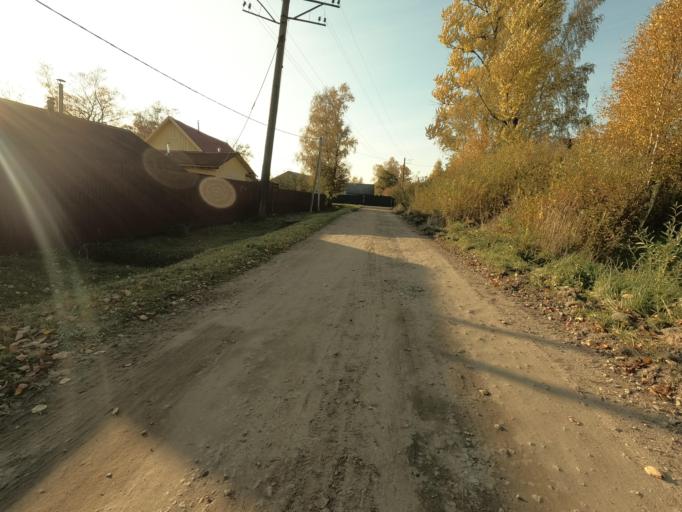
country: RU
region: Leningrad
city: Mga
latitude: 59.7547
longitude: 31.0565
